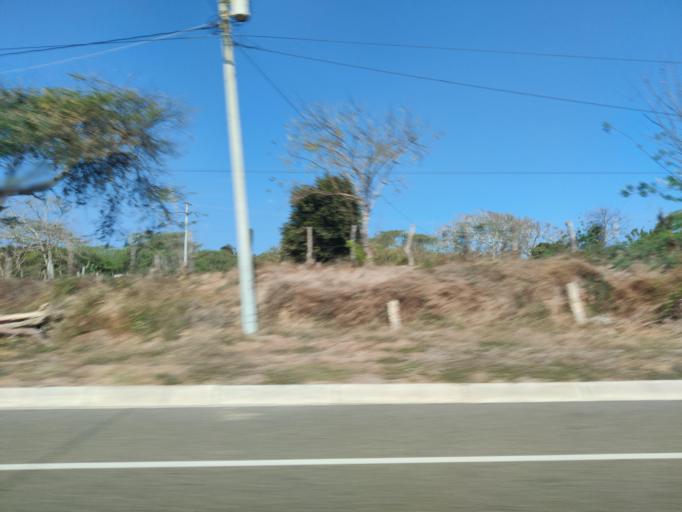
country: CO
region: Atlantico
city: Puerto Colombia
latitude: 10.9644
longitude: -74.9981
